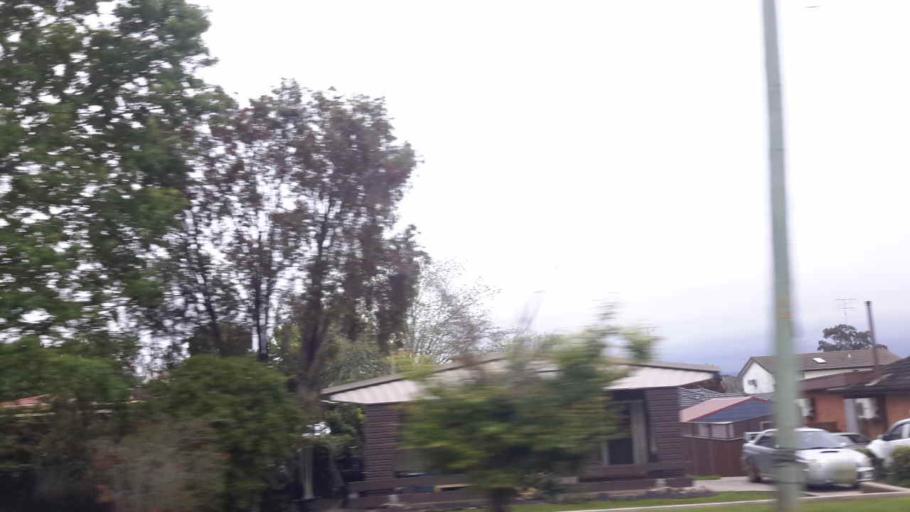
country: AU
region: New South Wales
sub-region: Penrith Municipality
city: Kingswood Park
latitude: -33.7635
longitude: 150.7099
